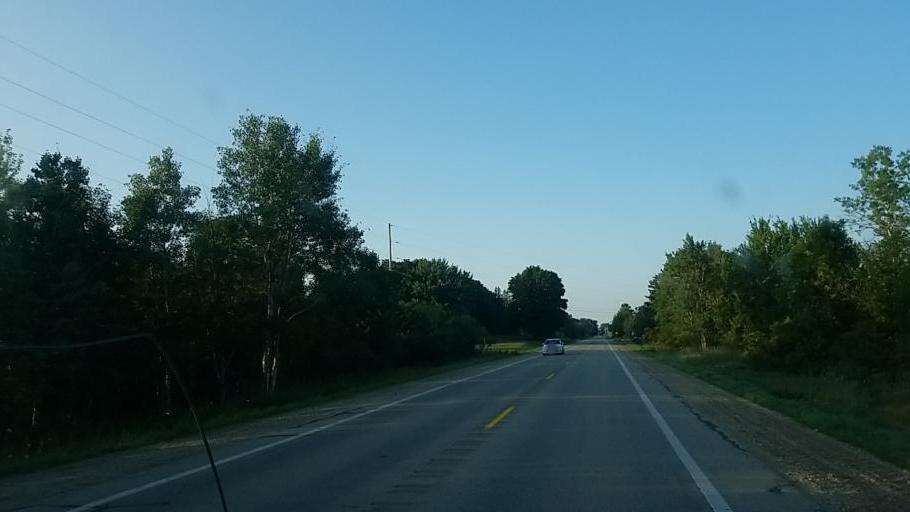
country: US
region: Michigan
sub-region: Isabella County
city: Lake Isabella
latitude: 43.6052
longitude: -85.1455
